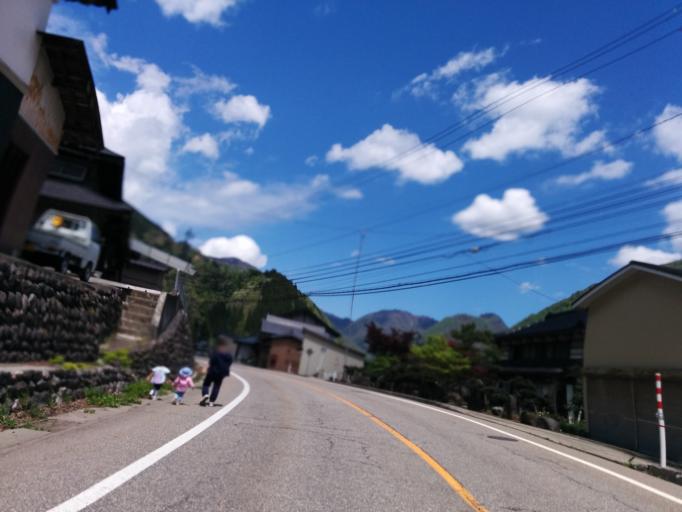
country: JP
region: Toyama
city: Fukumitsu
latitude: 36.3785
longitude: 136.8712
